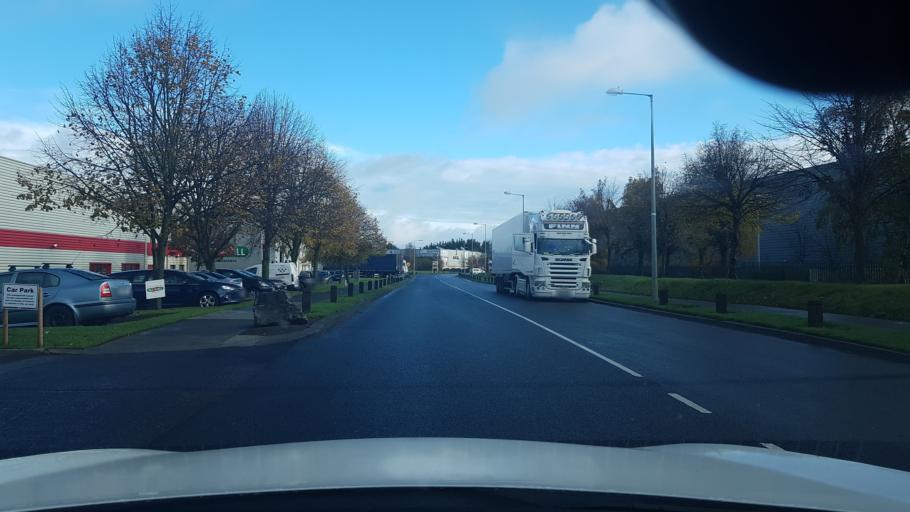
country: IE
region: Leinster
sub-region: Fingal County
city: Blanchardstown
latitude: 53.4034
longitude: -6.3553
